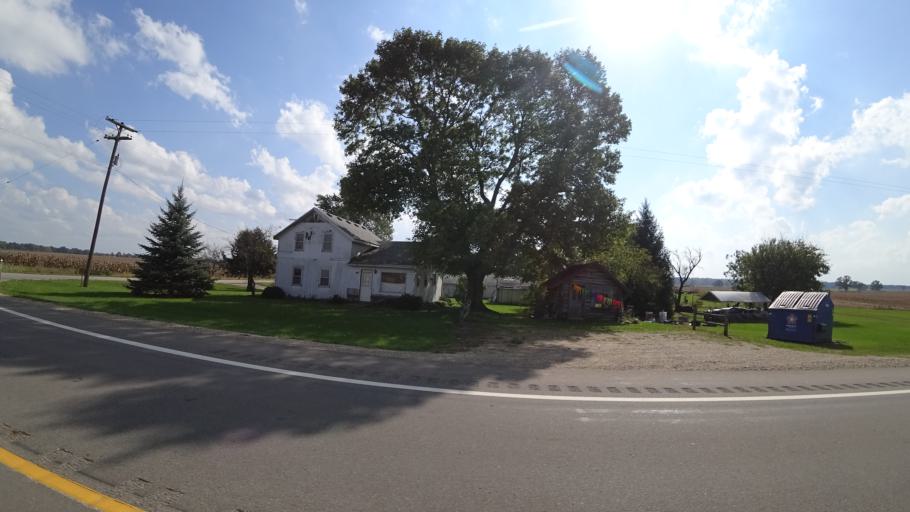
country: US
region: Michigan
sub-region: Calhoun County
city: Athens
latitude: 42.0577
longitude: -85.2742
